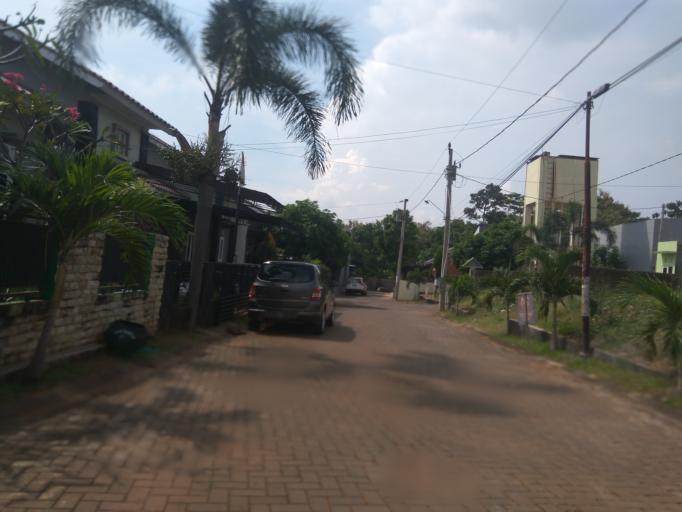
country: ID
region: Central Java
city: Mranggen
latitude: -7.0675
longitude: 110.4492
